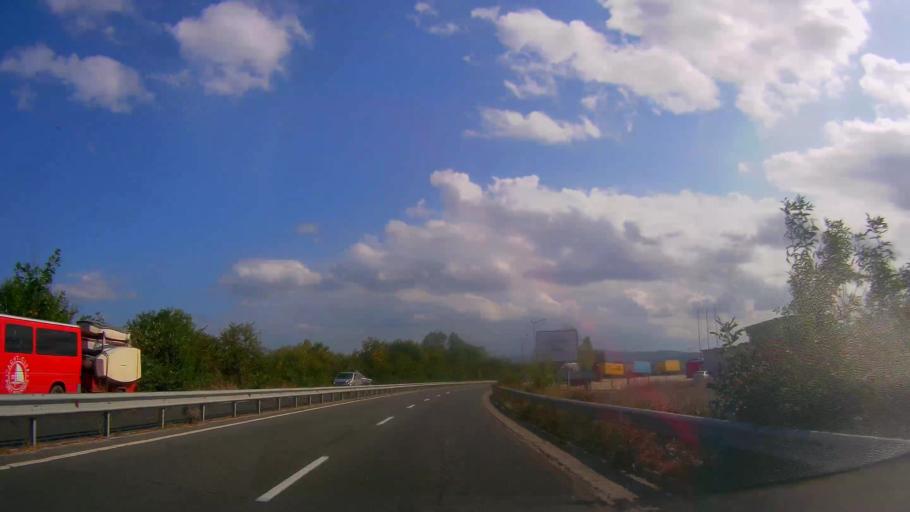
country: BG
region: Burgas
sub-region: Obshtina Sozopol
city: Chernomorets
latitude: 42.4377
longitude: 27.6367
